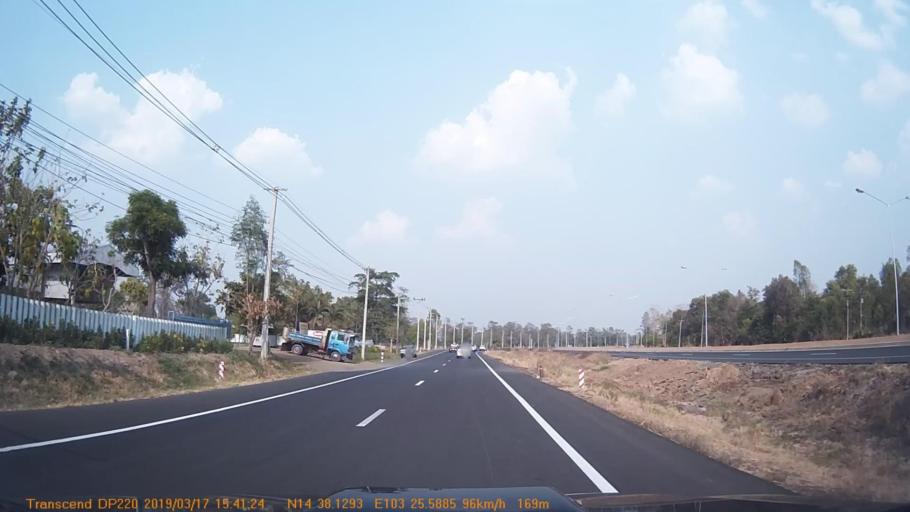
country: TH
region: Surin
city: Prasat
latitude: 14.6356
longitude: 103.4269
